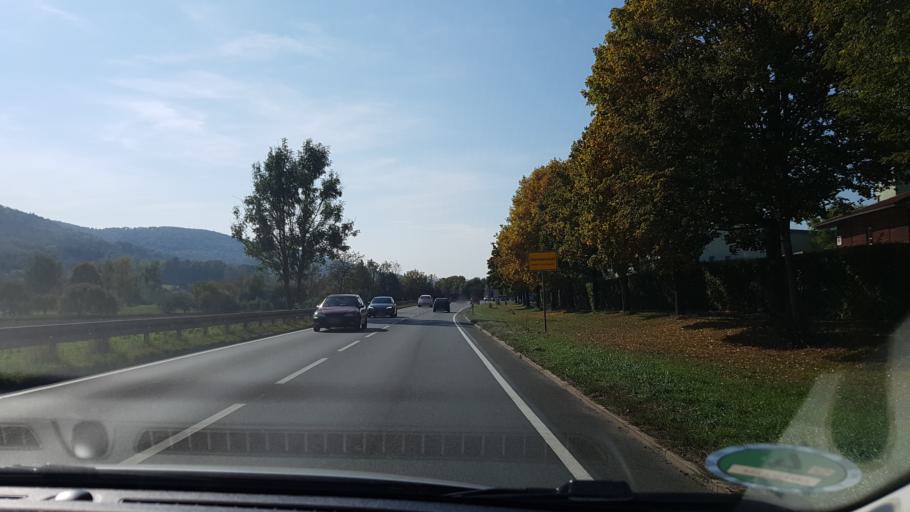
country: DE
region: Bavaria
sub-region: Upper Franconia
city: Ebermannstadt
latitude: 49.7880
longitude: 11.1915
